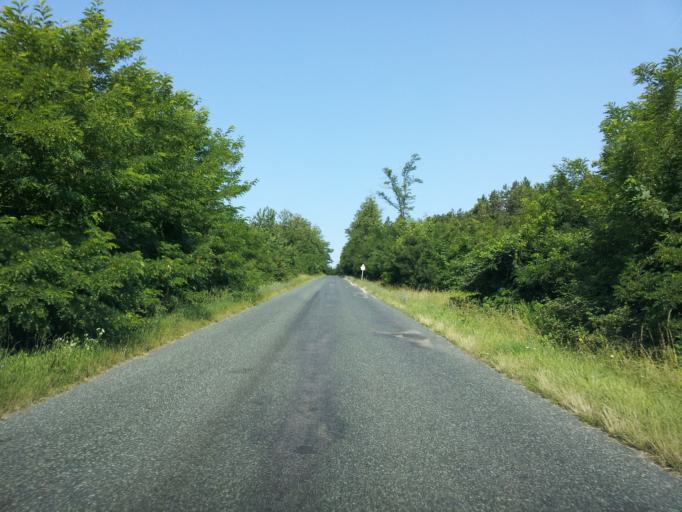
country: HU
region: Zala
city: Heviz
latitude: 46.8662
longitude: 17.1542
